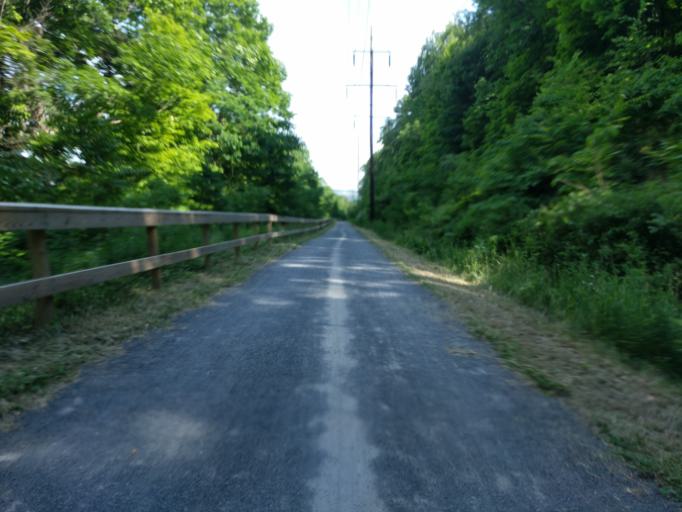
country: US
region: New York
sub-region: Tompkins County
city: Northwest Ithaca
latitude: 42.4566
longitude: -76.5194
